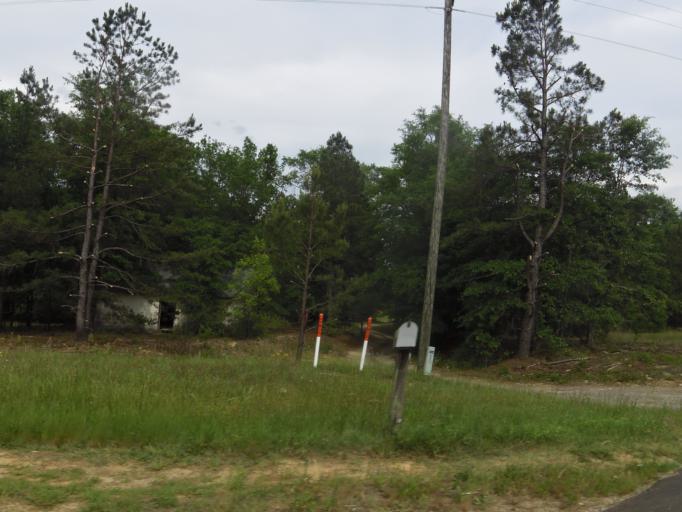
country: US
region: Georgia
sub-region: McDuffie County
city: Thomson
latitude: 33.3942
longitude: -82.4755
